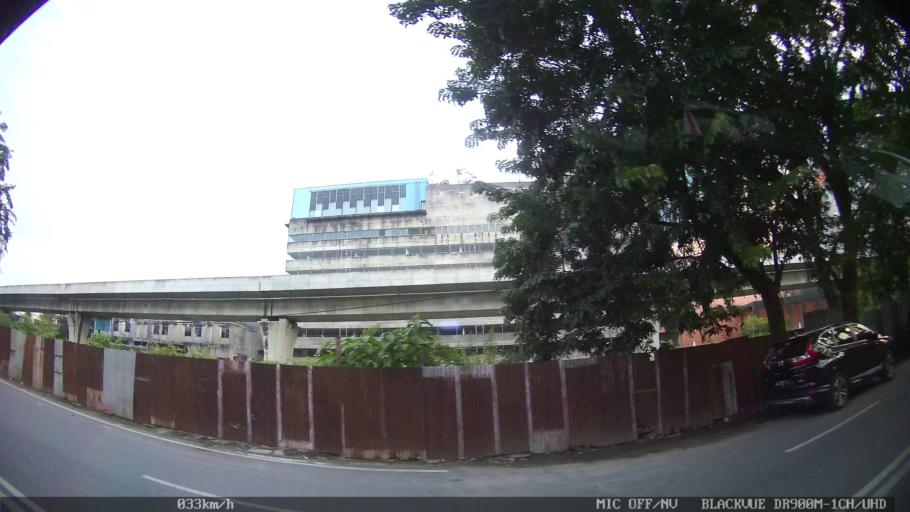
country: ID
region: North Sumatra
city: Medan
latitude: 3.5874
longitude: 98.6926
